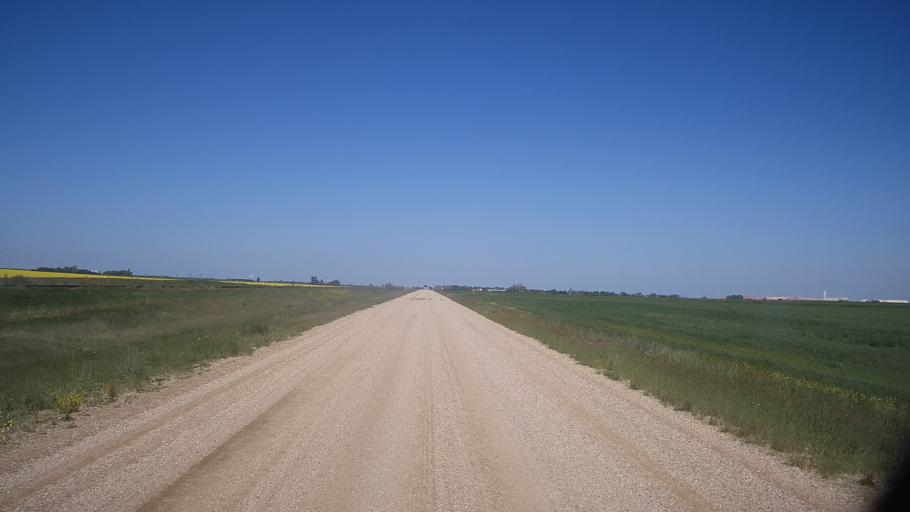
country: CA
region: Saskatchewan
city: Watrous
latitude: 51.8795
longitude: -106.0183
